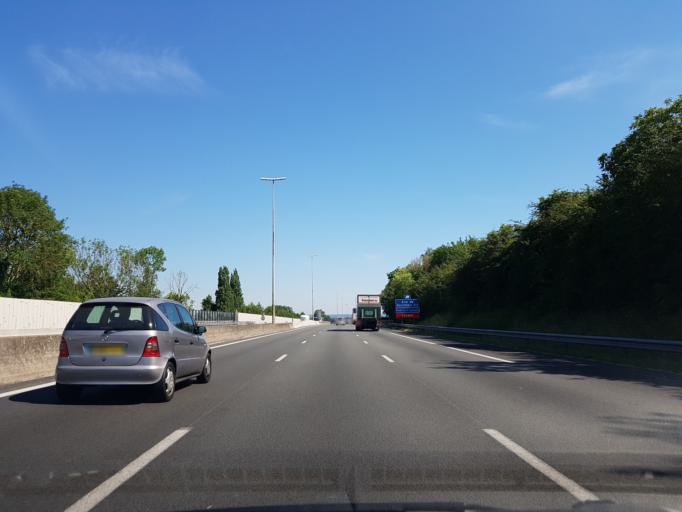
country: FR
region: Ile-de-France
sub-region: Departement du Val-d'Oise
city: Survilliers
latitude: 49.0987
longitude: 2.5502
